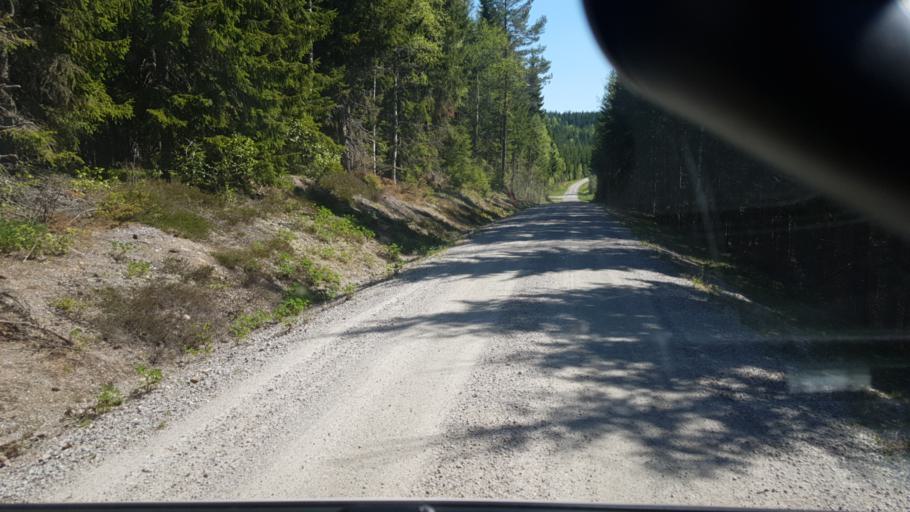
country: SE
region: Vaermland
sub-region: Arvika Kommun
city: Arvika
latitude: 59.8280
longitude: 12.8367
